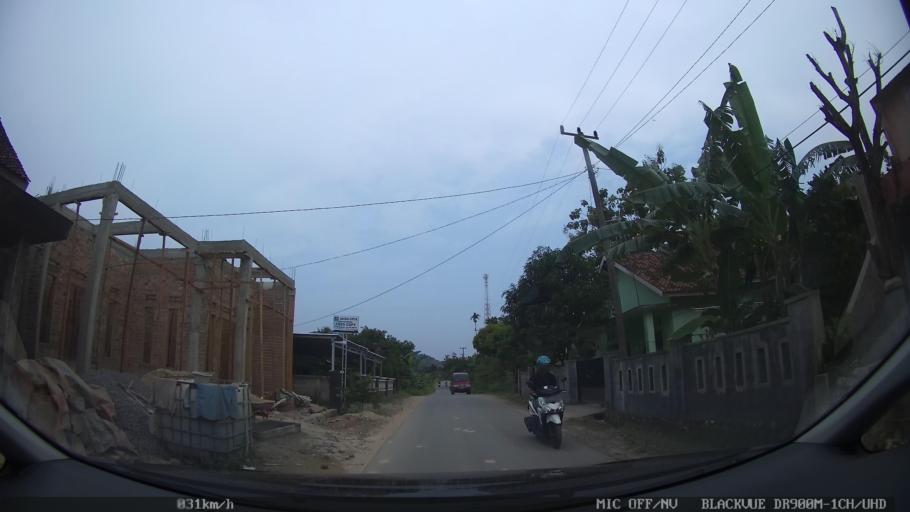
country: ID
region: Lampung
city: Panjang
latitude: -5.4183
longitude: 105.3493
